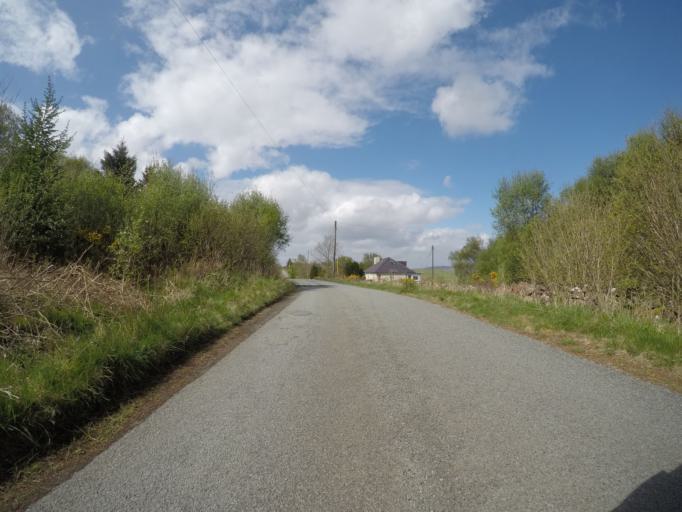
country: GB
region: Scotland
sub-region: Highland
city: Isle of Skye
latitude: 57.4618
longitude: -6.3299
